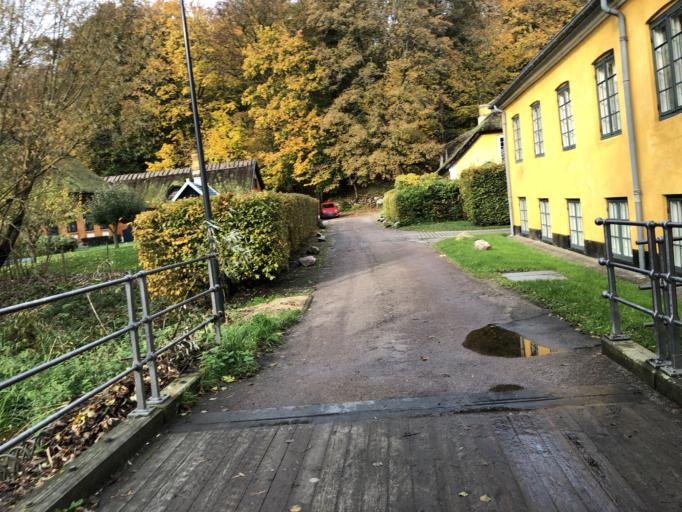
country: DK
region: Capital Region
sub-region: Lyngby-Tarbaek Kommune
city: Kongens Lyngby
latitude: 55.8020
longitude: 12.5143
